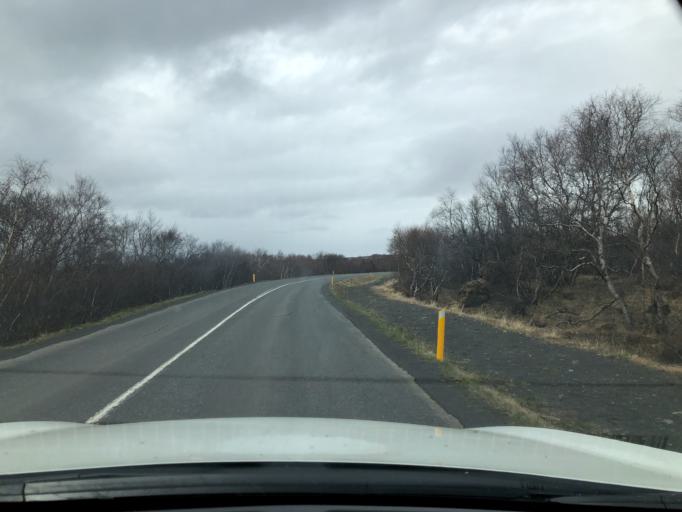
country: IS
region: Northeast
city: Laugar
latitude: 65.6301
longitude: -16.9187
